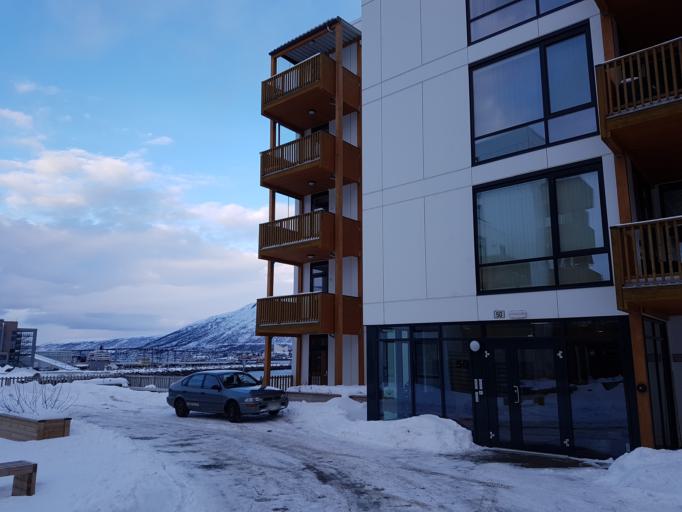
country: NO
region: Troms
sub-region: Tromso
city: Tromso
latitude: 69.6412
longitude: 18.9436
